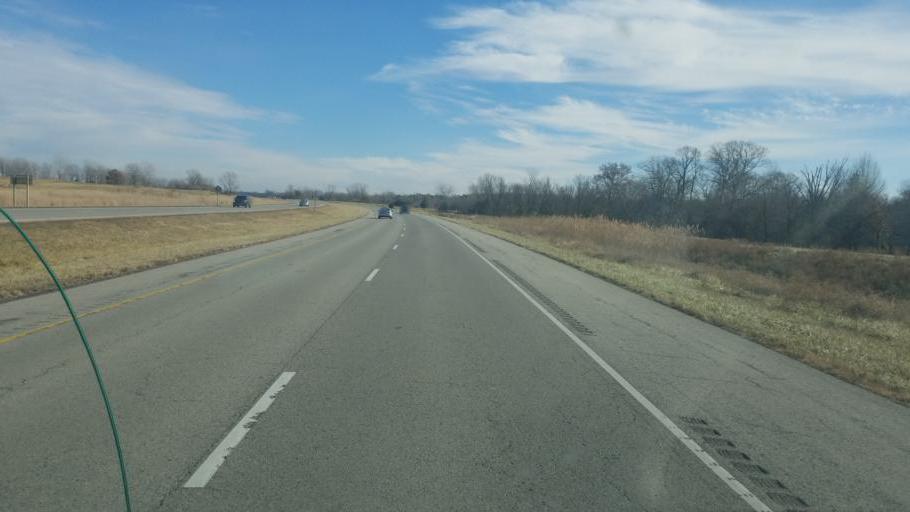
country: US
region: Illinois
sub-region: Williamson County
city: Marion
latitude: 37.7310
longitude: -88.7880
